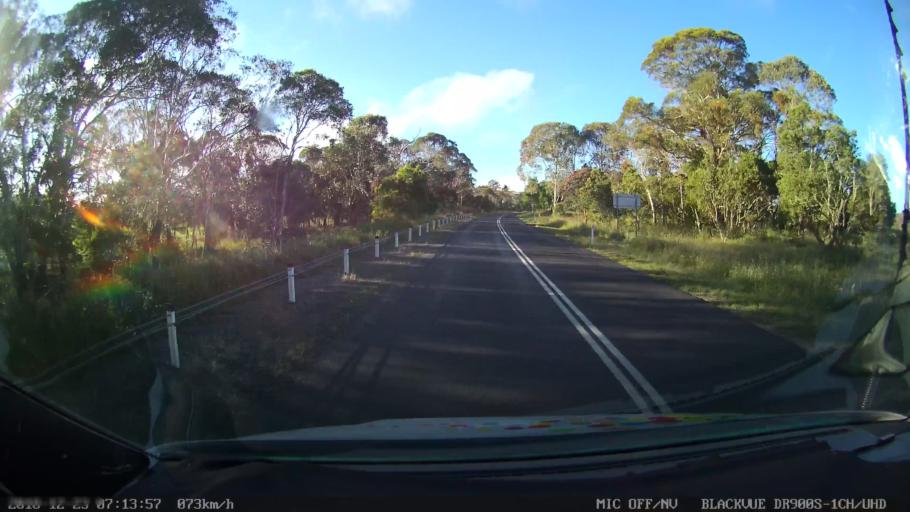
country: AU
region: New South Wales
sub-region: Bellingen
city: Dorrigo
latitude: -30.4299
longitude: 152.3247
